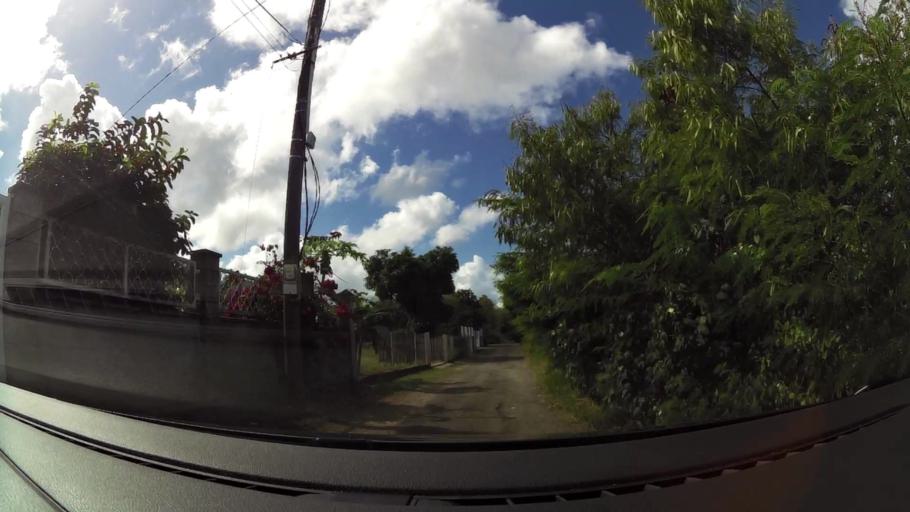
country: GP
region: Guadeloupe
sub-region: Guadeloupe
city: Port-Louis
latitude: 16.4245
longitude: -61.5229
